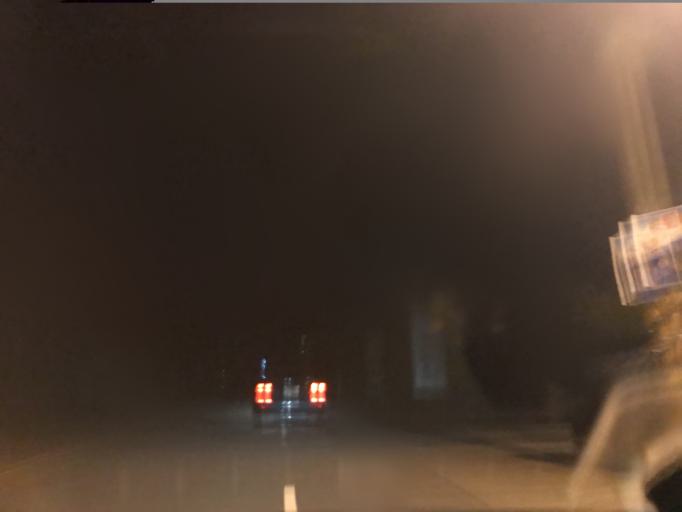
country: TW
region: Taiwan
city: Daxi
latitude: 24.8301
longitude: 121.1921
